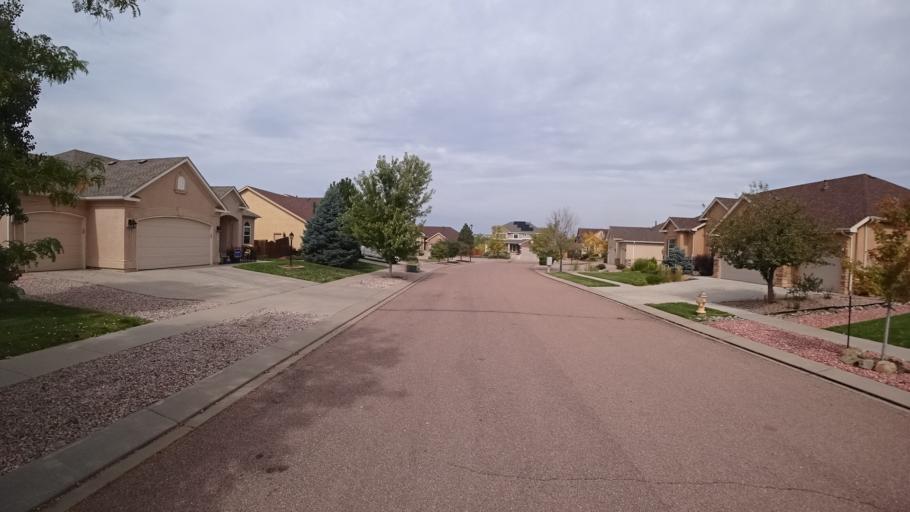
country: US
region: Colorado
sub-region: El Paso County
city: Cimarron Hills
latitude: 38.9160
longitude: -104.6965
